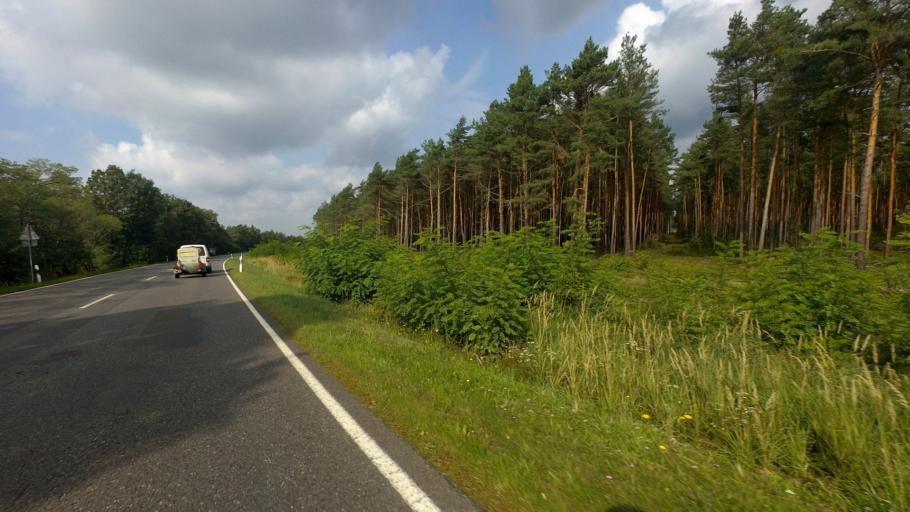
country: DE
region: Brandenburg
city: Elsterwerda
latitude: 51.4880
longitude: 13.4825
